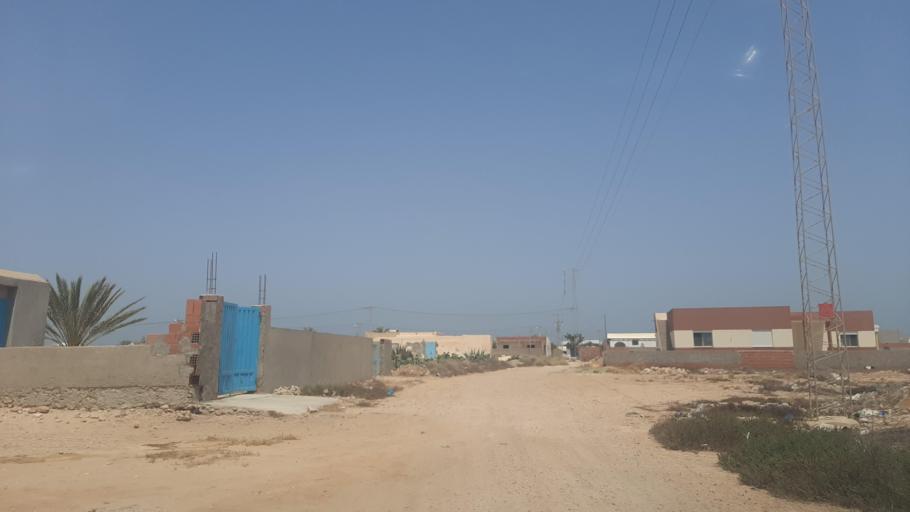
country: TN
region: Safaqis
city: Jabinyanah
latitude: 34.8213
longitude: 11.2548
